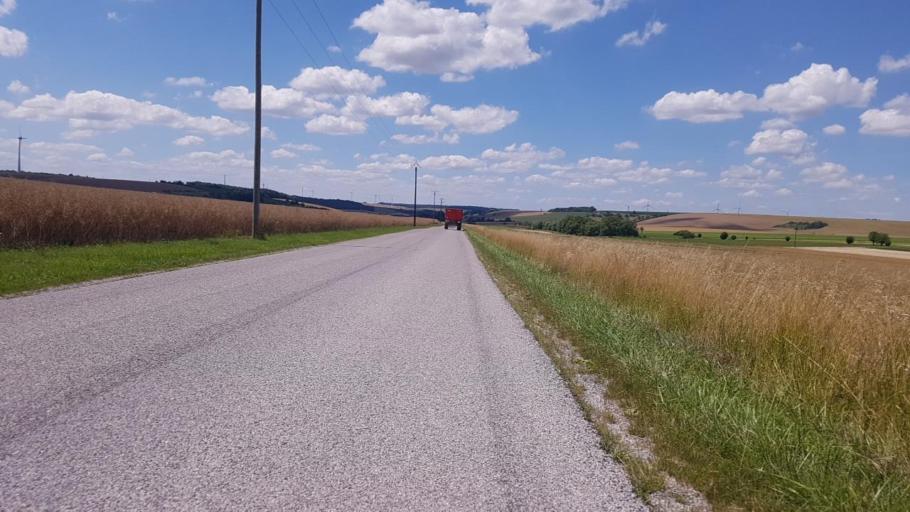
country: FR
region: Lorraine
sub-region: Departement de la Meuse
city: Vacon
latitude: 48.6551
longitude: 5.5354
